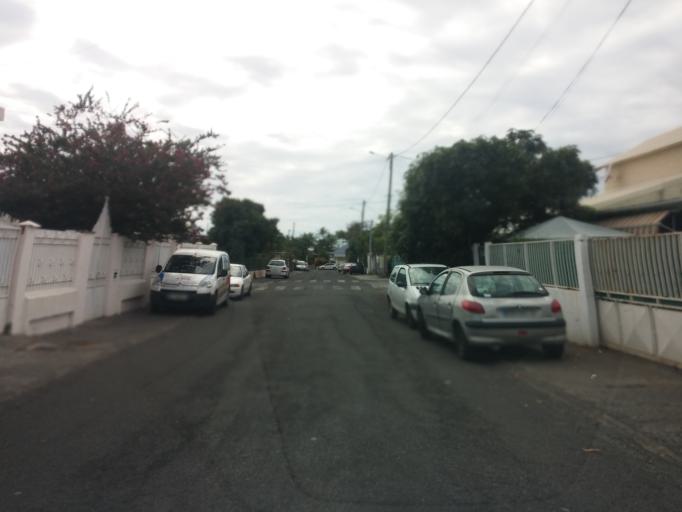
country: RE
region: Reunion
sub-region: Reunion
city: Le Port
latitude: -20.9417
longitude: 55.2905
